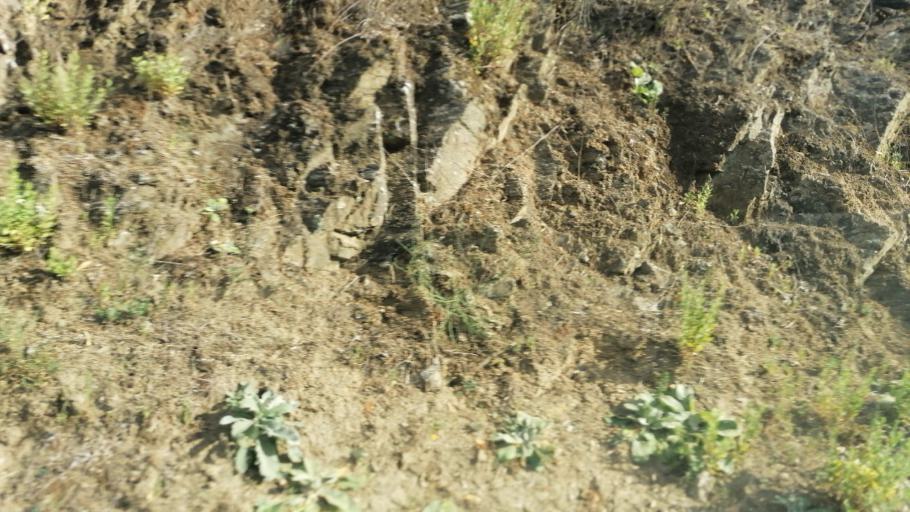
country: PT
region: Viseu
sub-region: Sao Joao da Pesqueira
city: Sao Joao da Pesqueira
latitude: 41.1426
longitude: -7.4243
